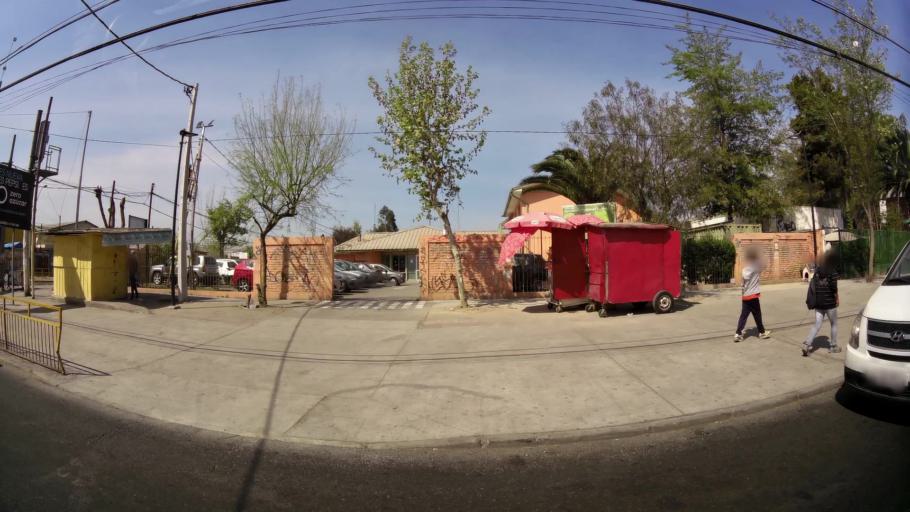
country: CL
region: Santiago Metropolitan
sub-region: Provincia de Santiago
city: Lo Prado
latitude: -33.4422
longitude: -70.7645
